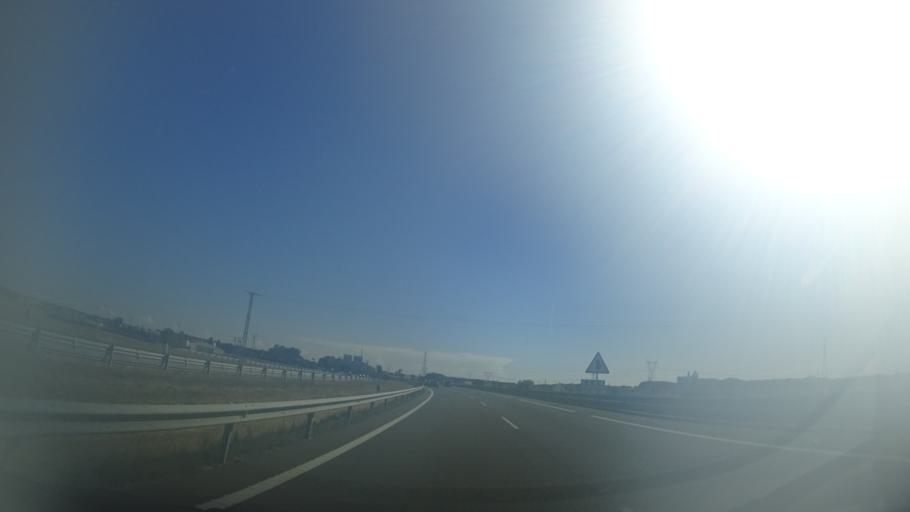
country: ES
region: Castille and Leon
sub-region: Provincia de Valladolid
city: Tordesillas
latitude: 41.4793
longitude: -4.9911
